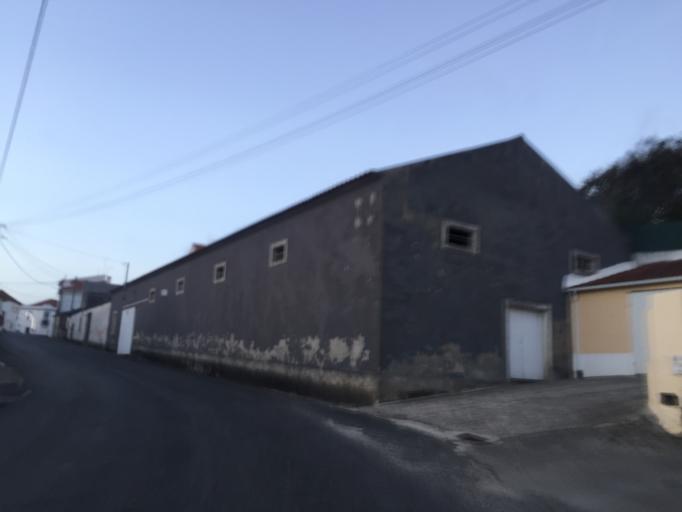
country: PT
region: Leiria
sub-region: Bombarral
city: Bombarral
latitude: 39.2860
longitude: -9.2144
